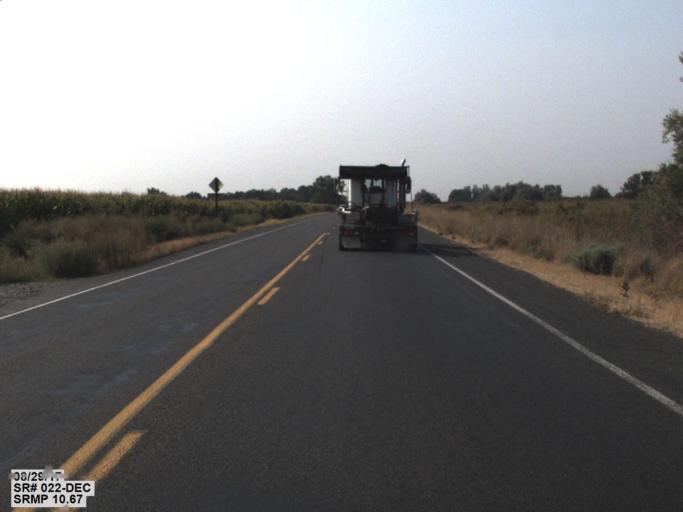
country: US
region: Washington
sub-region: Yakima County
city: Granger
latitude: 46.3111
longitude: -120.2113
